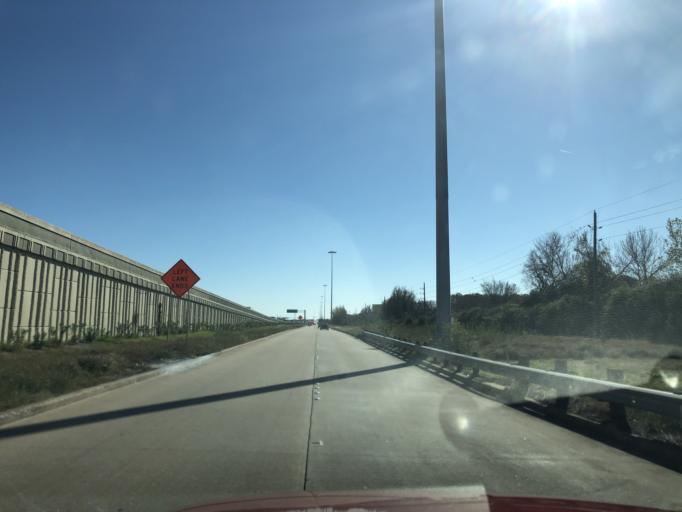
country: US
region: Texas
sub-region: Harris County
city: Cypress
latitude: 29.9615
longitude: -95.6878
